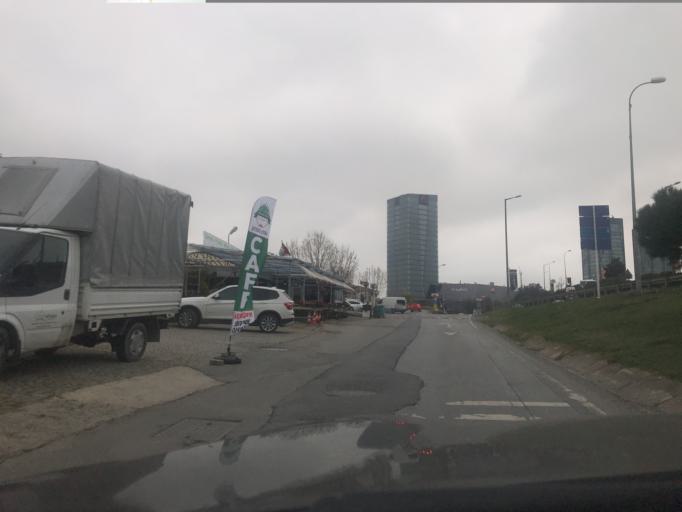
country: TR
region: Istanbul
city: Umraniye
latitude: 41.0292
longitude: 29.1331
